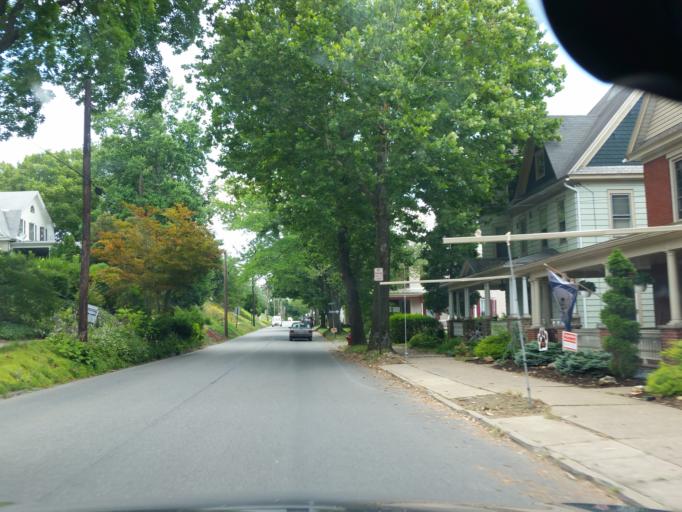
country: US
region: Pennsylvania
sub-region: Northumberland County
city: Milton
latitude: 41.0205
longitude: -76.8473
